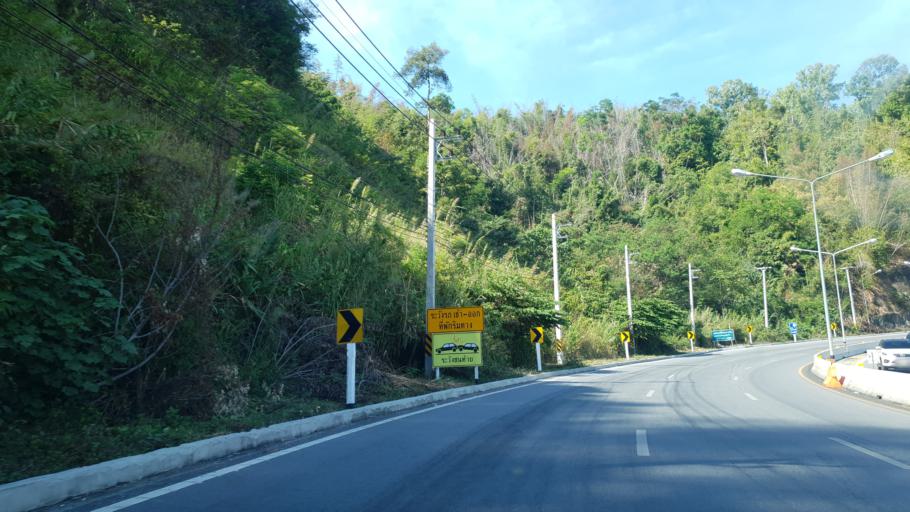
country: TH
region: Phrae
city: Den Chai
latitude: 17.8316
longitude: 100.0590
